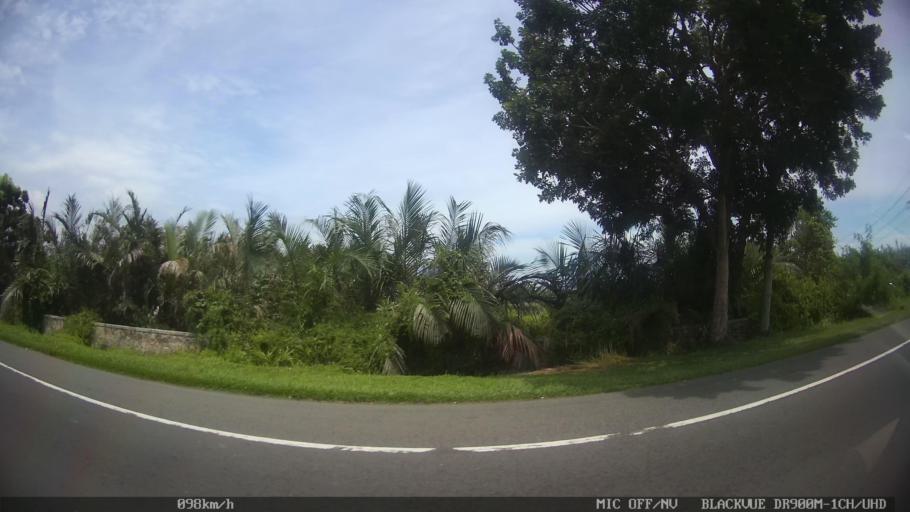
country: ID
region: North Sumatra
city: Labuhan Deli
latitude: 3.7464
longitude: 98.6801
